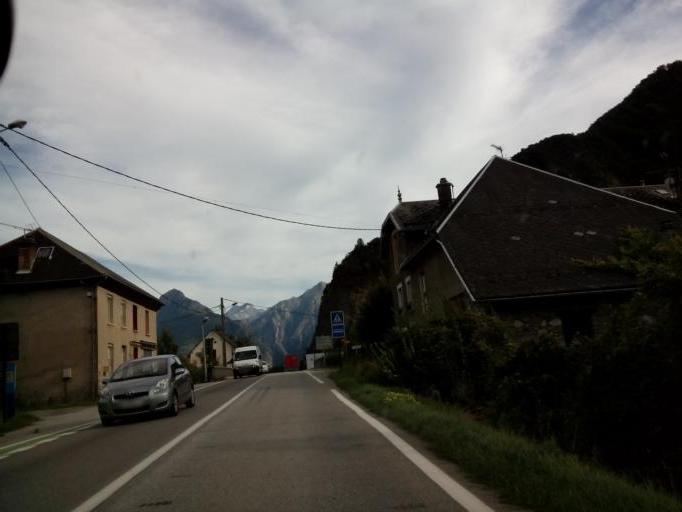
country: FR
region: Rhone-Alpes
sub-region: Departement de l'Isere
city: Huez
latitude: 45.0747
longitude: 6.0160
